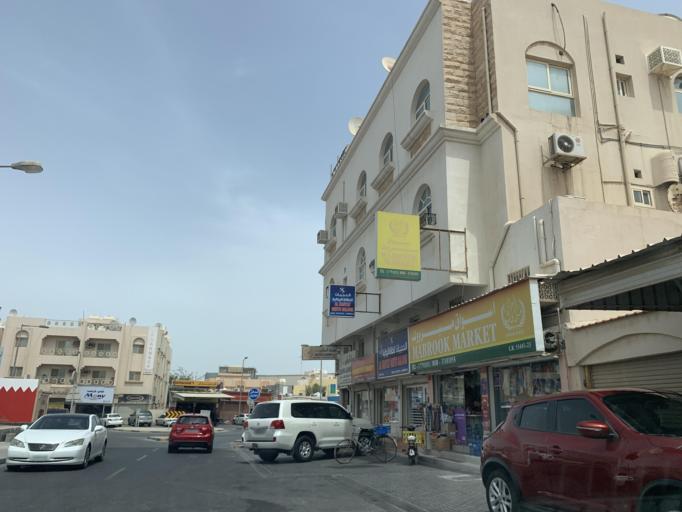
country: BH
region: Northern
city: Ar Rifa'
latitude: 26.1326
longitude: 50.5645
